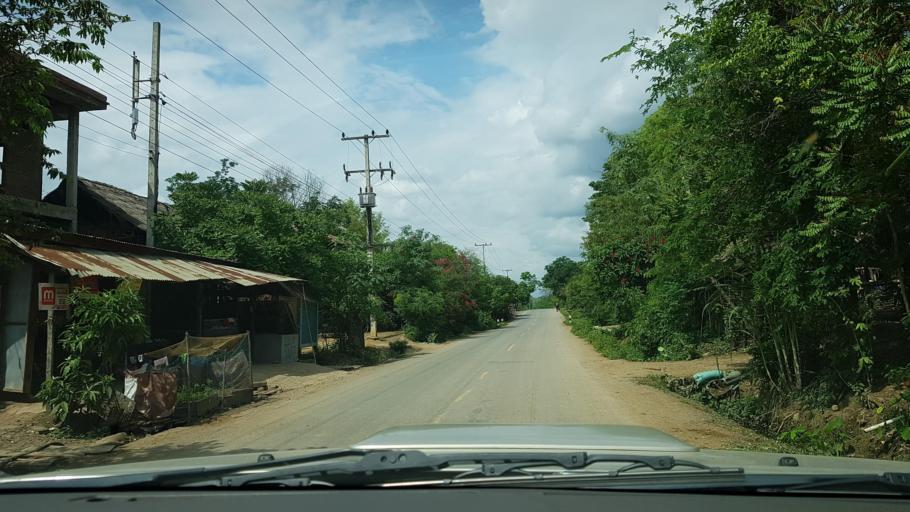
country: LA
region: Loungnamtha
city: Muang Nale
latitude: 20.2651
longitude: 101.5953
